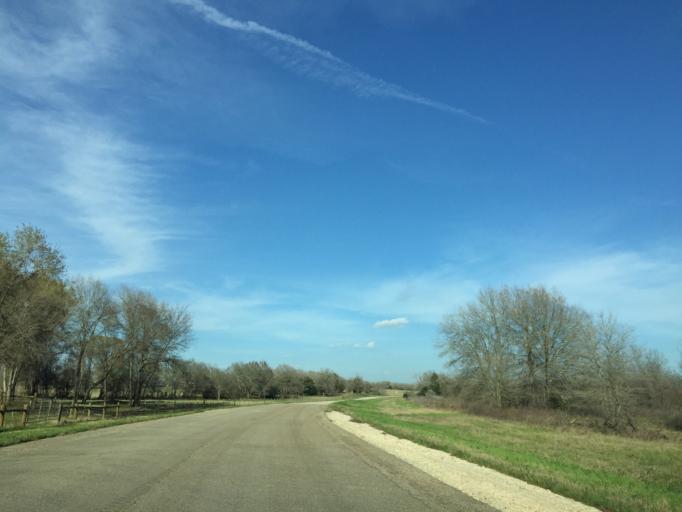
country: US
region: Texas
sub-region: Lee County
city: Lexington
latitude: 30.4585
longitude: -97.1536
